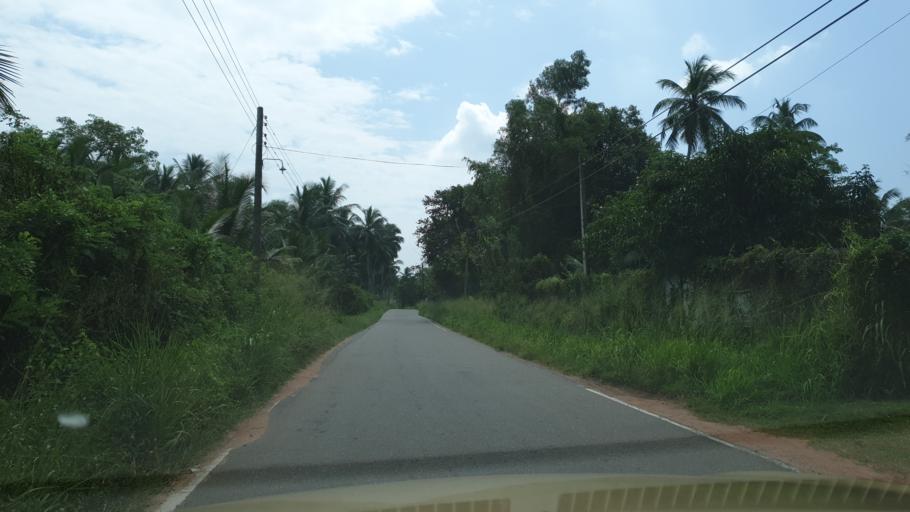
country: LK
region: North Western
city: Kuliyapitiya
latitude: 7.3607
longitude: 79.9672
